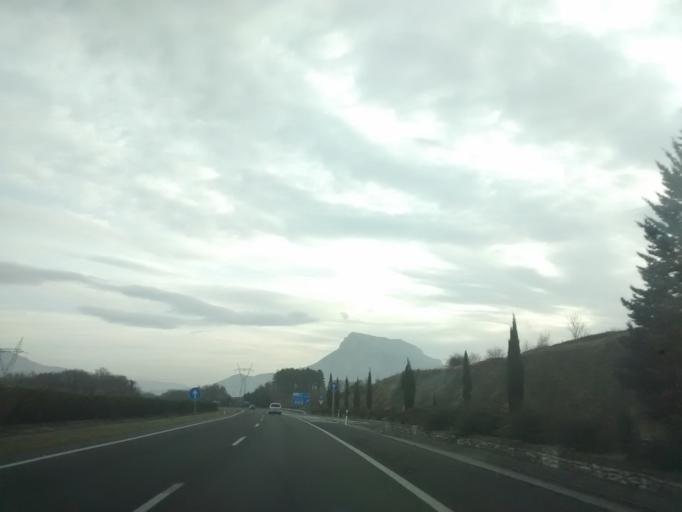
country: ES
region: Navarre
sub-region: Provincia de Navarra
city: Bakaiku
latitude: 42.8929
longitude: -2.0946
